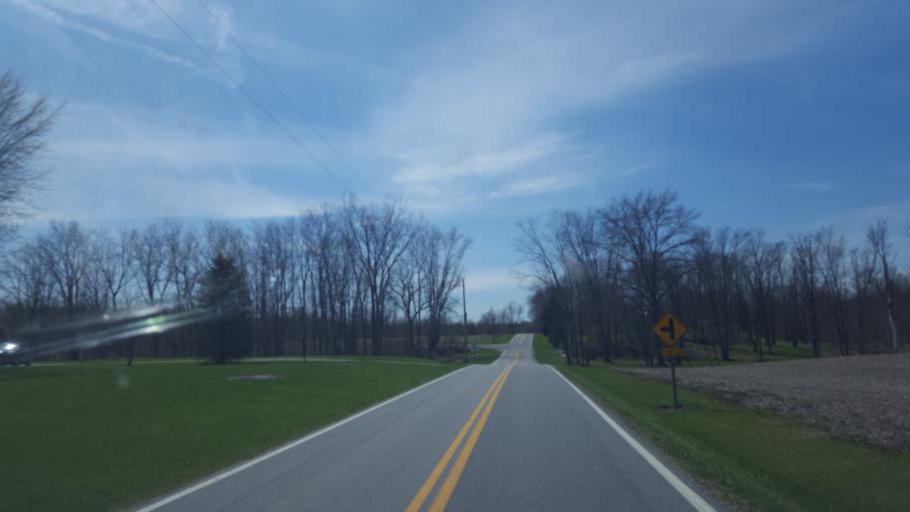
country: US
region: Ohio
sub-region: Delaware County
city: Ashley
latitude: 40.4009
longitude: -83.0314
